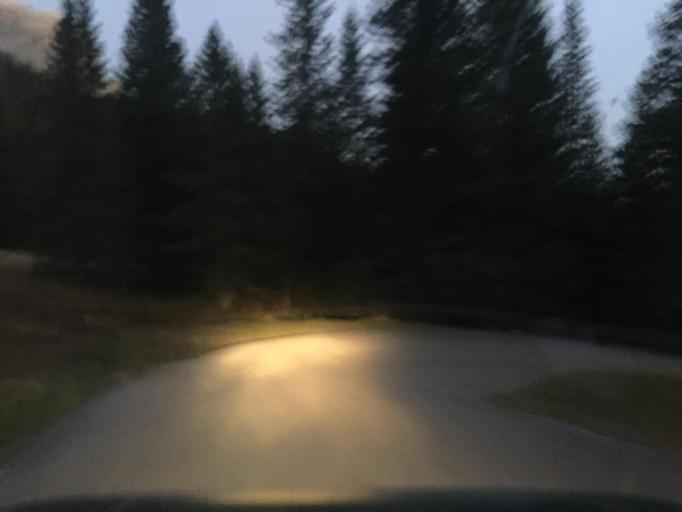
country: IT
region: Friuli Venezia Giulia
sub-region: Provincia di Udine
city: Forni Avoltri
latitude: 46.6160
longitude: 12.7241
